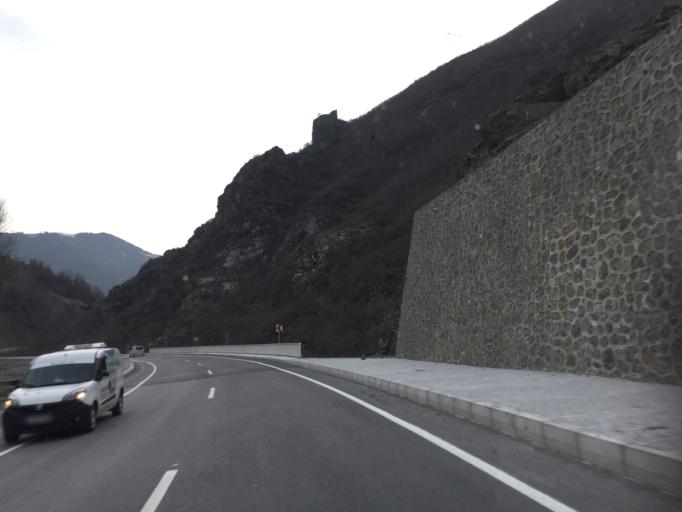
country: TR
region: Trabzon
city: Macka
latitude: 40.7714
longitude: 39.5654
